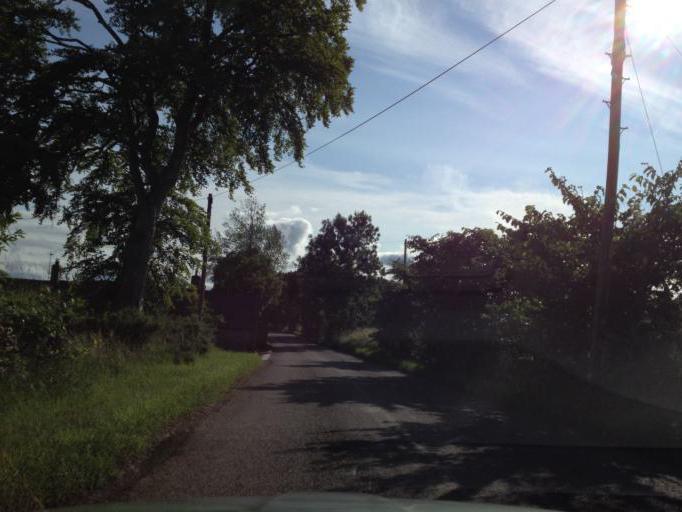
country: GB
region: Scotland
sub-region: Angus
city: Brechin
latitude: 56.8384
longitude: -2.6168
